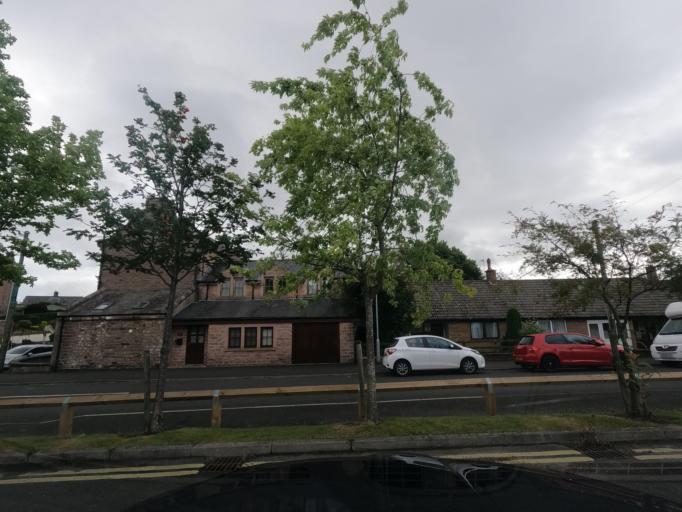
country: GB
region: England
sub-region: Northumberland
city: Wooler
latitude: 55.5471
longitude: -2.0186
